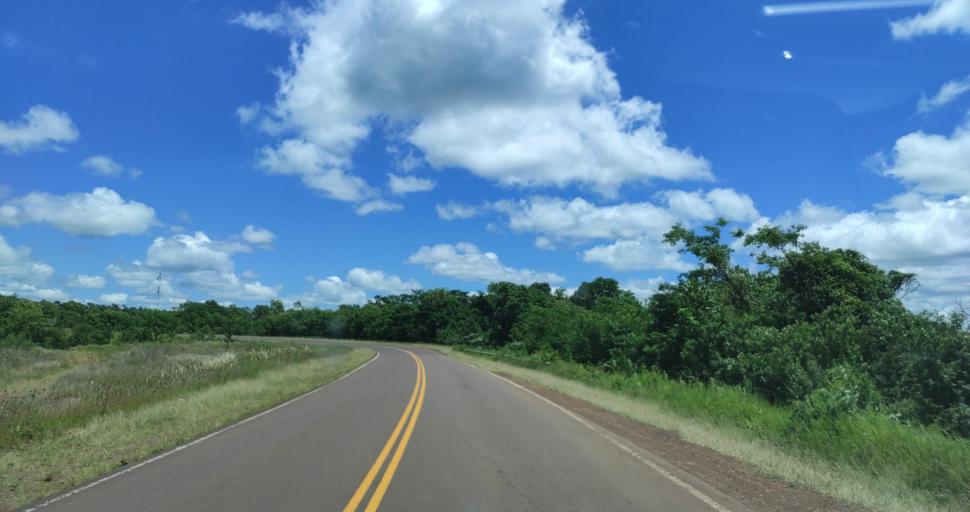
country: AR
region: Misiones
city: Cerro Azul
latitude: -27.5601
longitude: -55.5051
